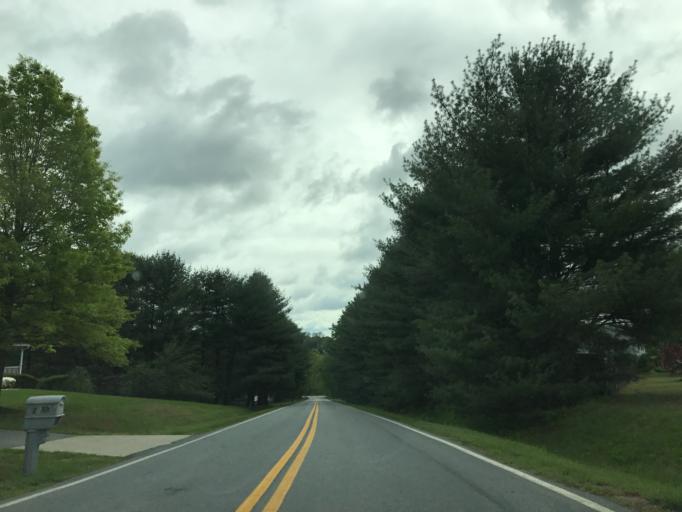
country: US
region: Maryland
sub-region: Baltimore County
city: Reisterstown
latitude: 39.4962
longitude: -76.9071
